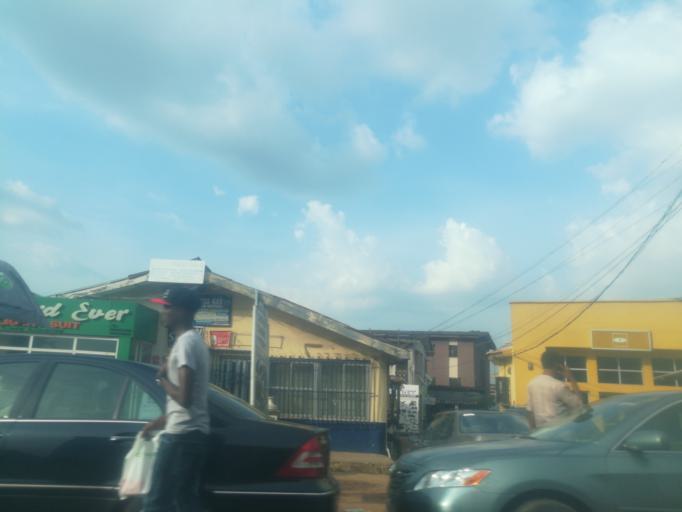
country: NG
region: Ogun
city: Abeokuta
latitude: 7.1360
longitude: 3.3347
